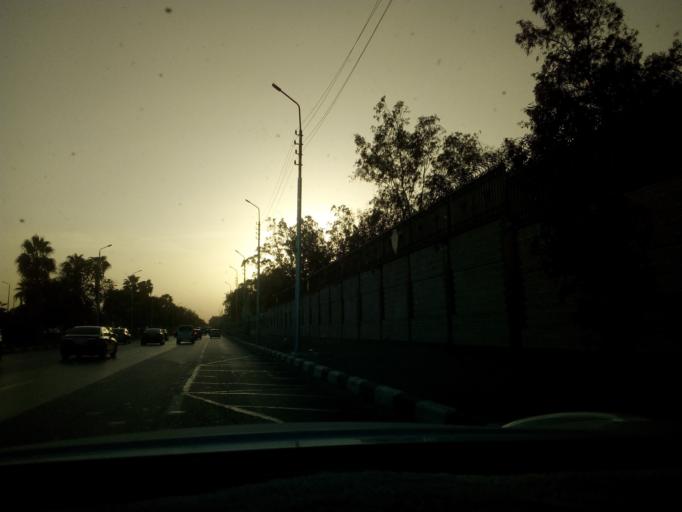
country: EG
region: Muhafazat al Qalyubiyah
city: Al Khankah
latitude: 30.1080
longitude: 31.3650
